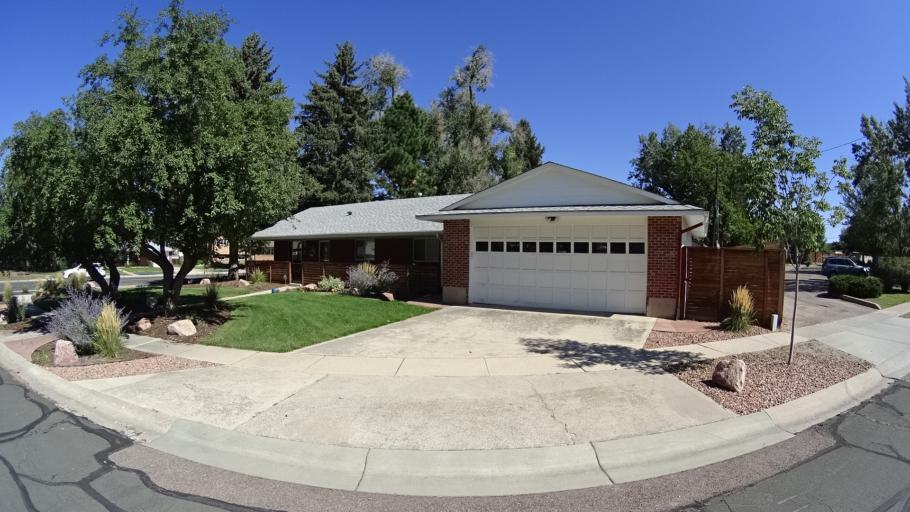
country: US
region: Colorado
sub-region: El Paso County
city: Colorado Springs
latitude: 38.8688
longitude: -104.7986
